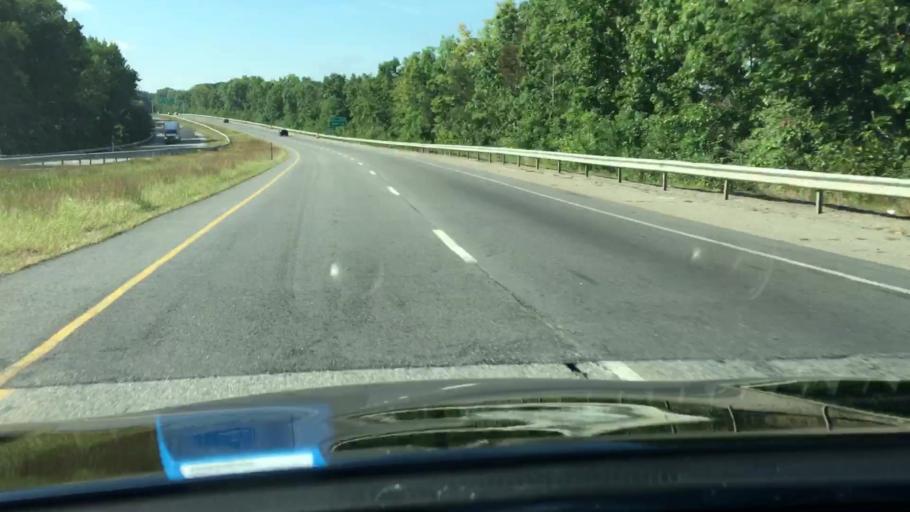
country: US
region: Connecticut
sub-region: Windham County
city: Danielson
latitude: 41.8095
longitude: -71.8718
